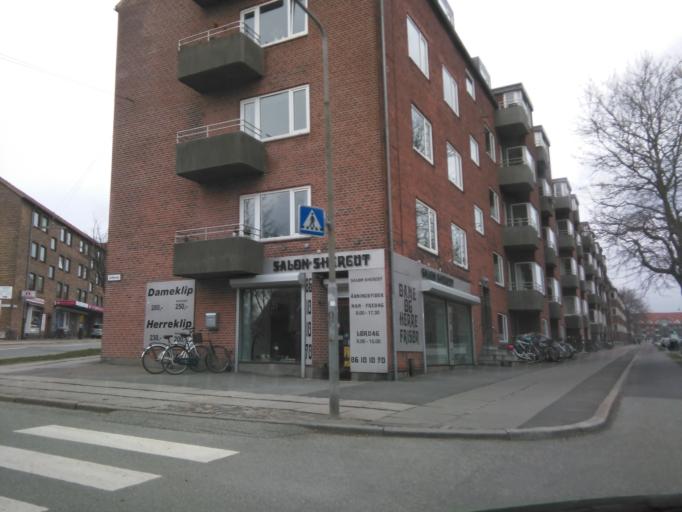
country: DK
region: Central Jutland
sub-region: Arhus Kommune
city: Arhus
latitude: 56.1723
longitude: 10.1998
